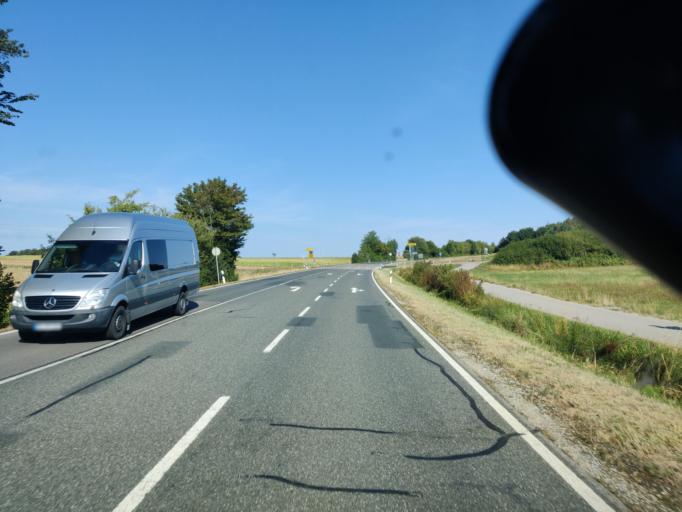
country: DE
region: Bavaria
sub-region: Regierungsbezirk Mittelfranken
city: Hilpoltstein
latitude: 49.1701
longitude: 11.2313
